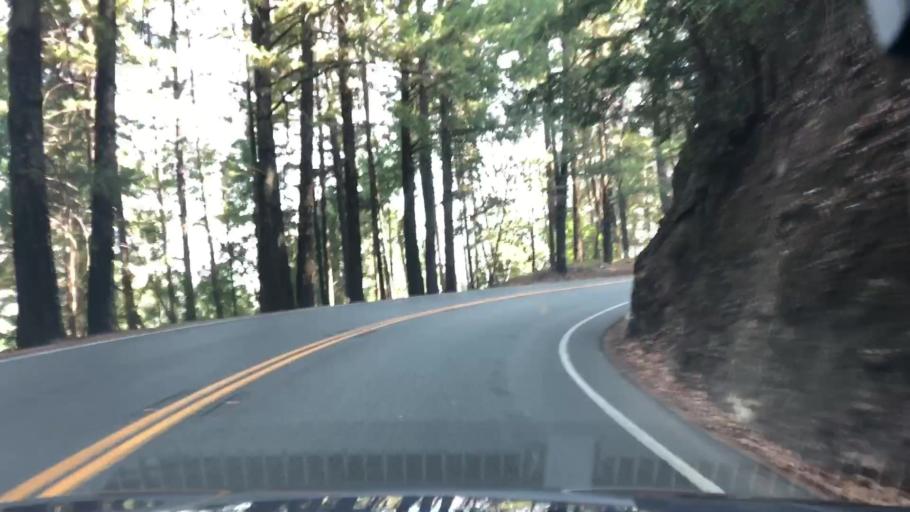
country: US
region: California
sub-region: Napa County
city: Calistoga
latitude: 38.6603
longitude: -122.5973
